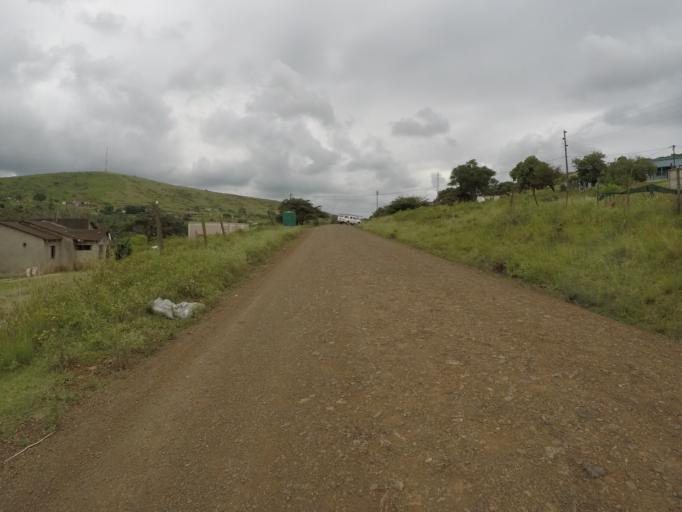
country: ZA
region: KwaZulu-Natal
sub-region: uThungulu District Municipality
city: Empangeni
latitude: -28.7067
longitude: 31.8483
